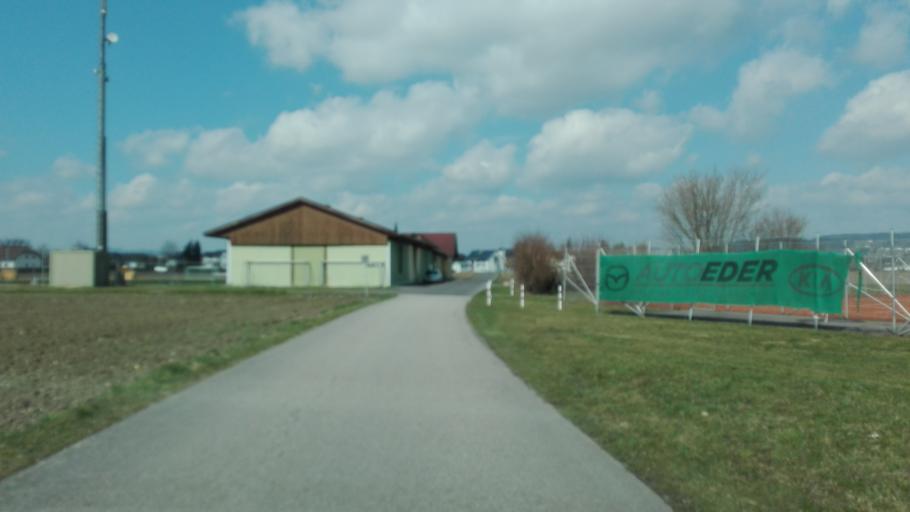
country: AT
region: Upper Austria
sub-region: Politischer Bezirk Urfahr-Umgebung
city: Goldworth
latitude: 48.3239
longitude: 14.1051
